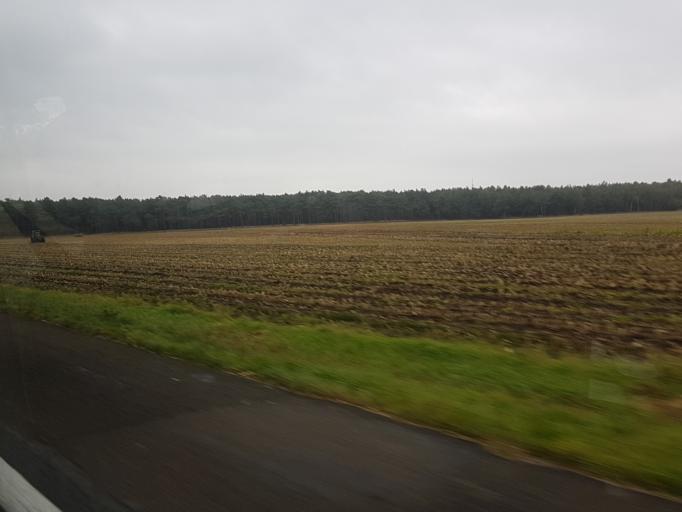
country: BE
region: Flanders
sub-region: Provincie Limburg
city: Lommel
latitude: 51.2202
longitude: 5.3341
